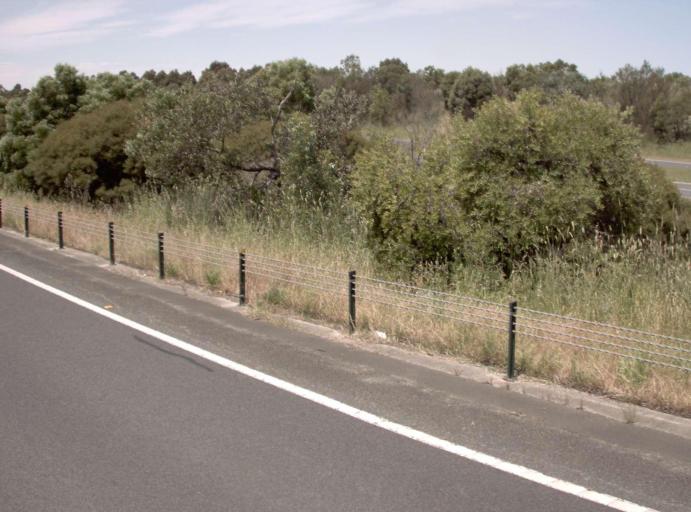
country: AU
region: Victoria
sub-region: Latrobe
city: Morwell
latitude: -38.2284
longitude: 146.4585
